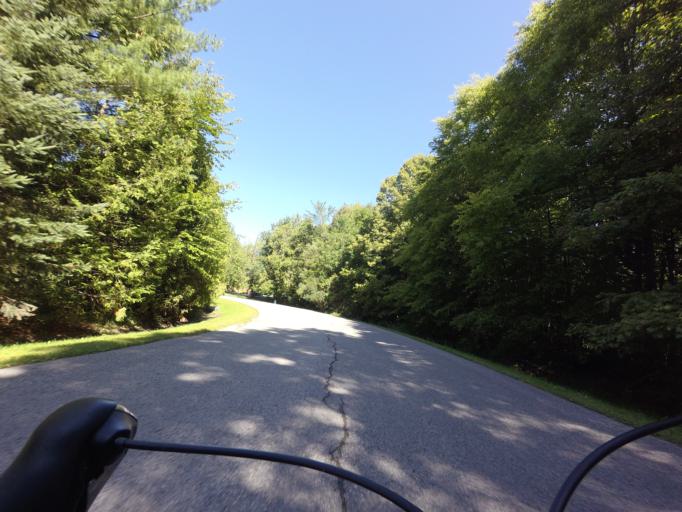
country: CA
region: Ontario
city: Bells Corners
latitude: 45.1774
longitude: -75.8252
